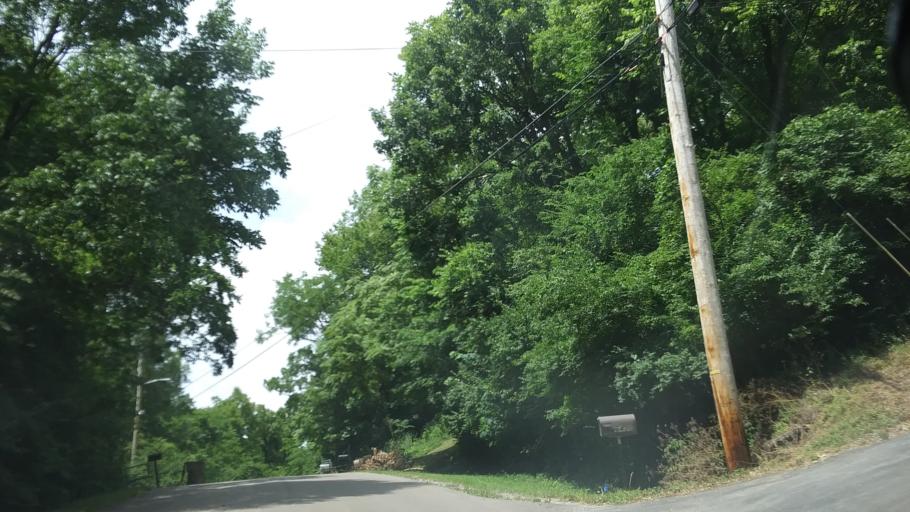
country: US
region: Tennessee
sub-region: Davidson County
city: Belle Meade
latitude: 36.1392
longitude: -86.8742
